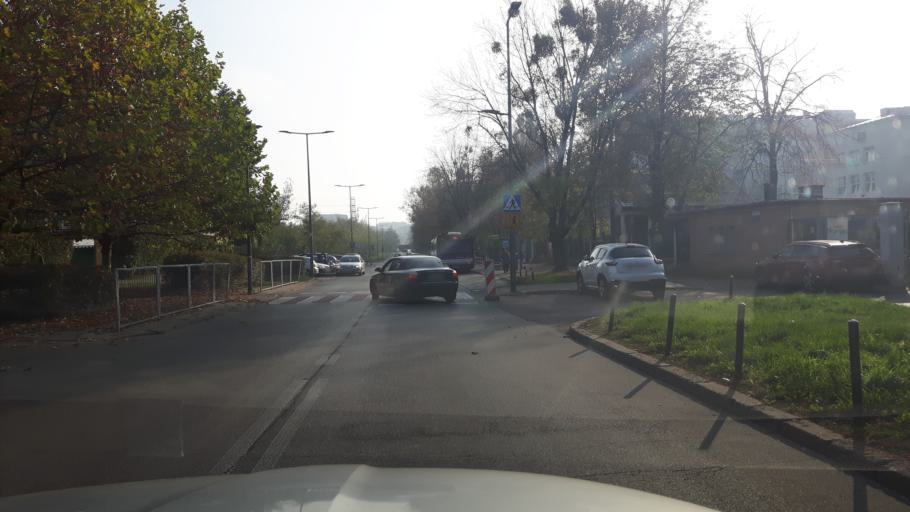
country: PL
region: Masovian Voivodeship
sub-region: Warszawa
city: Ochota
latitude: 52.1920
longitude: 20.9955
